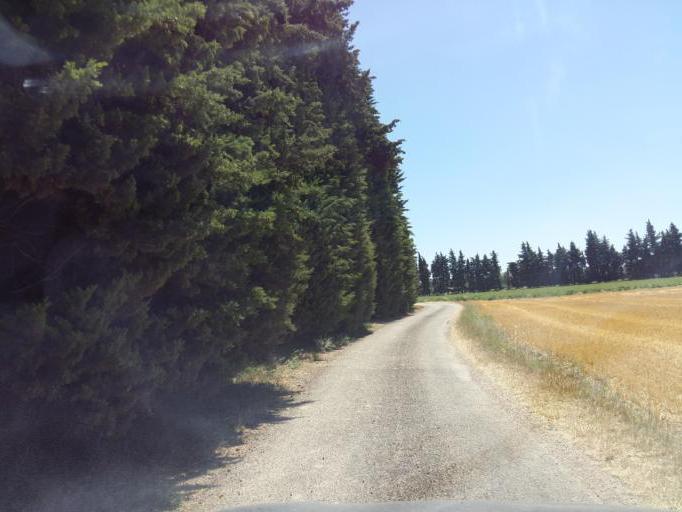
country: FR
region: Provence-Alpes-Cote d'Azur
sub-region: Departement du Vaucluse
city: Orange
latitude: 44.1550
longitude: 4.7872
